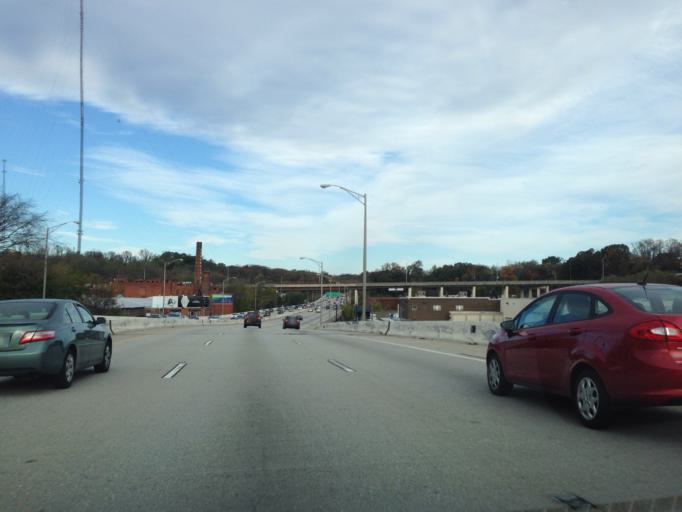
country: US
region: Maryland
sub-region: City of Baltimore
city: Baltimore
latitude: 39.3320
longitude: -76.6422
